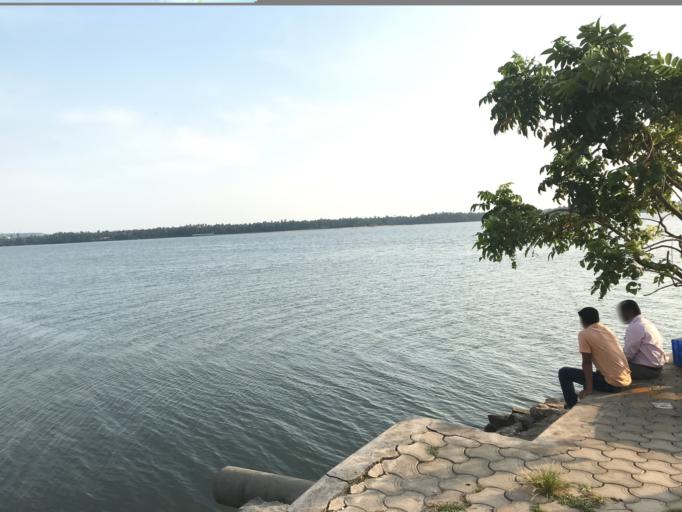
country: IN
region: Karnataka
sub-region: Dakshina Kannada
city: Ullal
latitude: 12.8430
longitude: 74.8423
